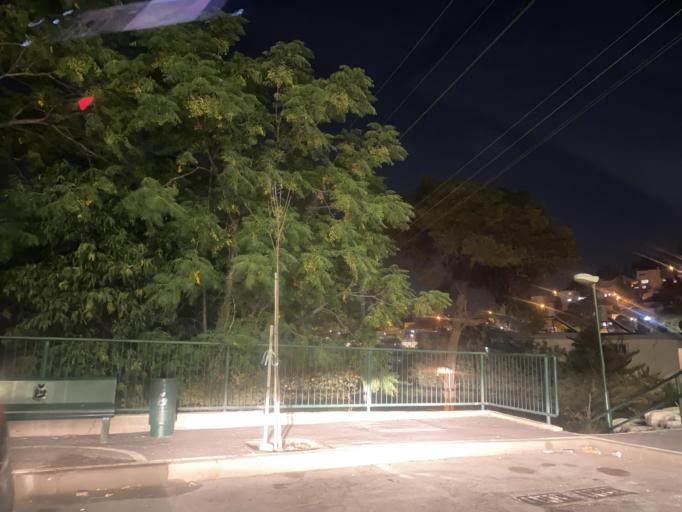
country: IL
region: Haifa
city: Daliyat el Karmil
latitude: 32.6568
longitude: 35.1046
